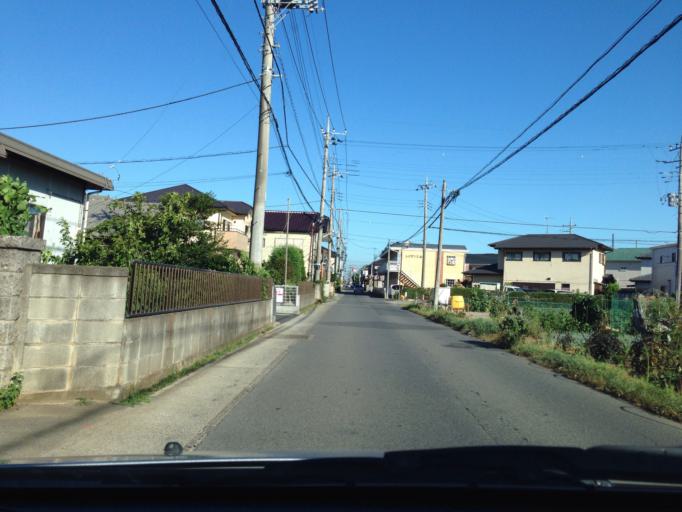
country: JP
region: Ibaraki
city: Naka
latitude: 36.0383
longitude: 140.1767
